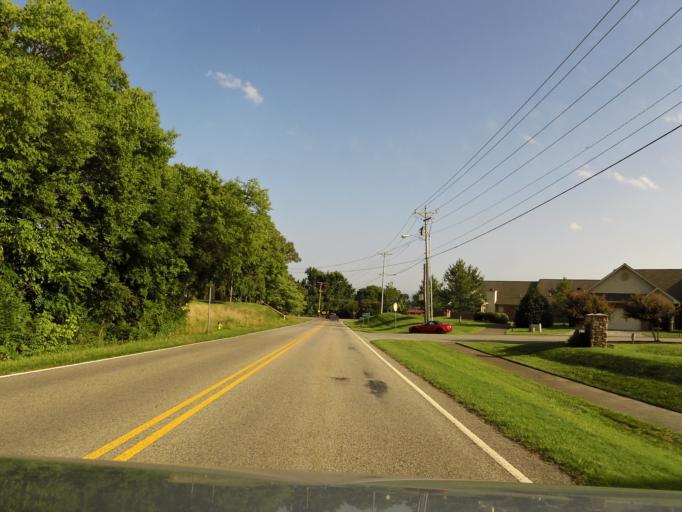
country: US
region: Tennessee
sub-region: Blount County
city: Eagleton Village
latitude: 35.7972
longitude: -83.9058
